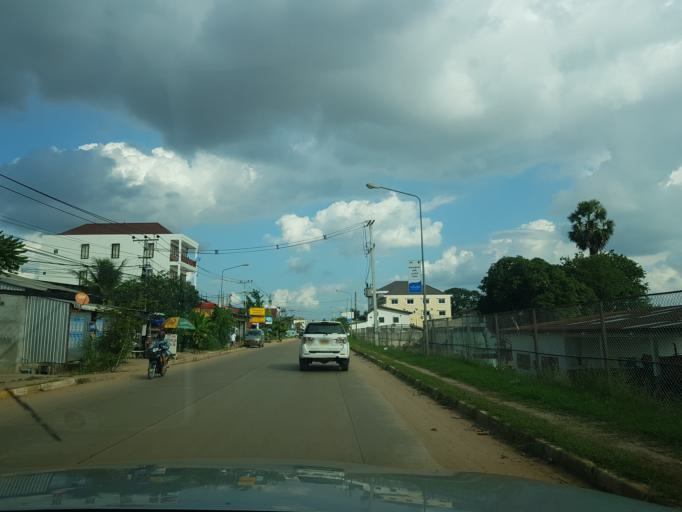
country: TH
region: Nong Khai
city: Si Chiang Mai
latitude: 17.9748
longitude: 102.5489
